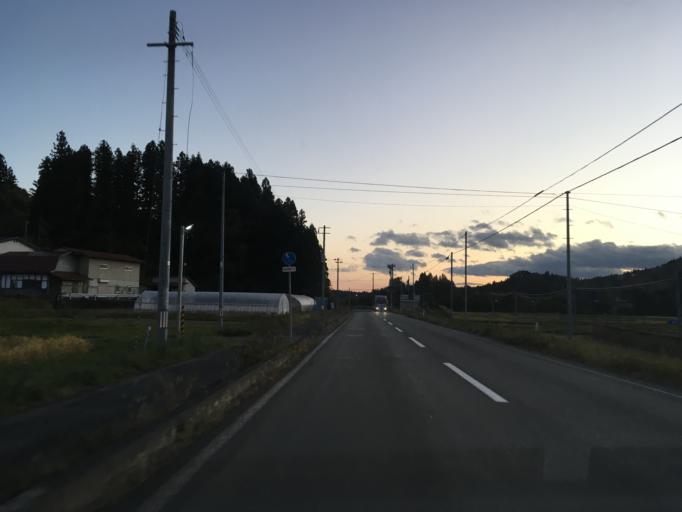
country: JP
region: Iwate
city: Kitakami
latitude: 39.2471
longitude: 141.2029
